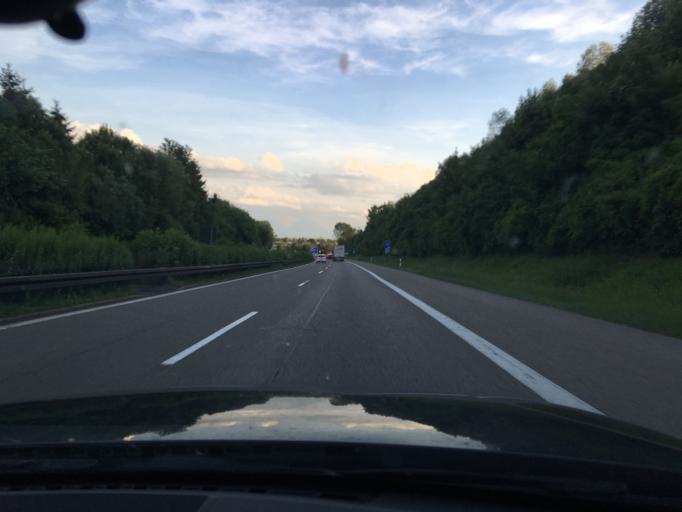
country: AT
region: Vorarlberg
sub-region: Politischer Bezirk Bregenz
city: Horbranz
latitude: 47.5570
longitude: 9.7351
